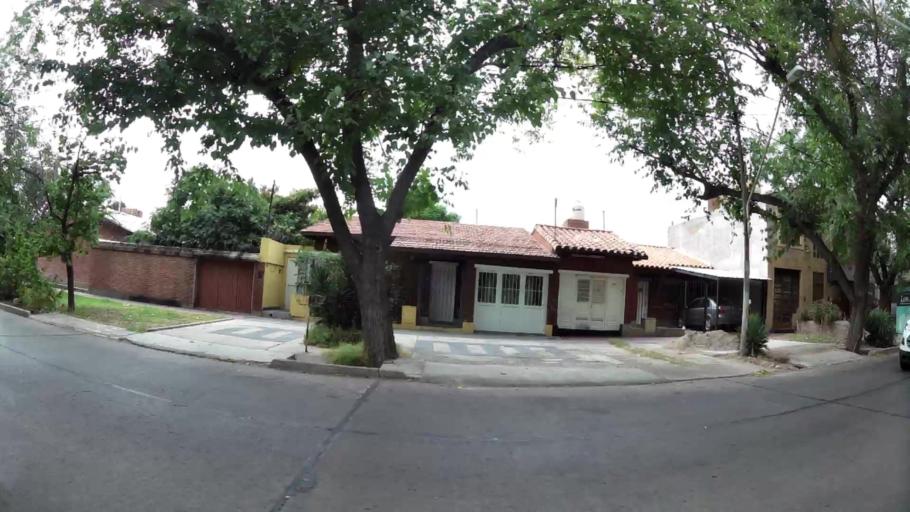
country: AR
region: Mendoza
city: Las Heras
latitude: -32.8725
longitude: -68.8553
